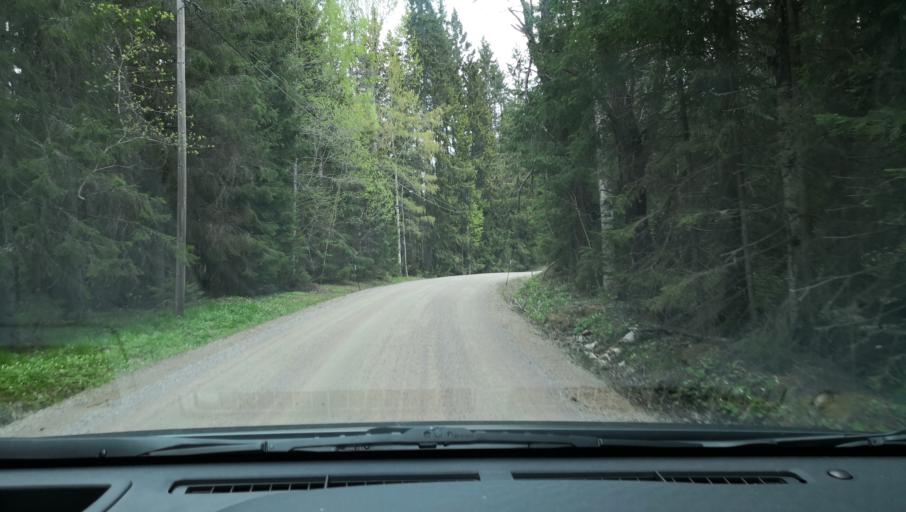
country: SE
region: Vaestmanland
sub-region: Fagersta Kommun
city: Fagersta
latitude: 60.0941
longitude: 15.7899
